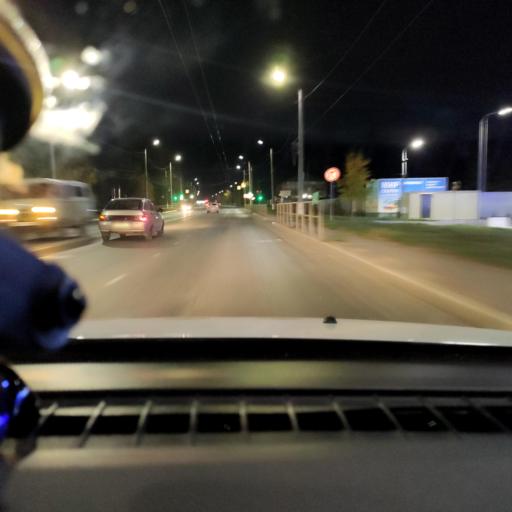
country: RU
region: Samara
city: Novokuybyshevsk
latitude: 53.0957
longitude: 49.9401
